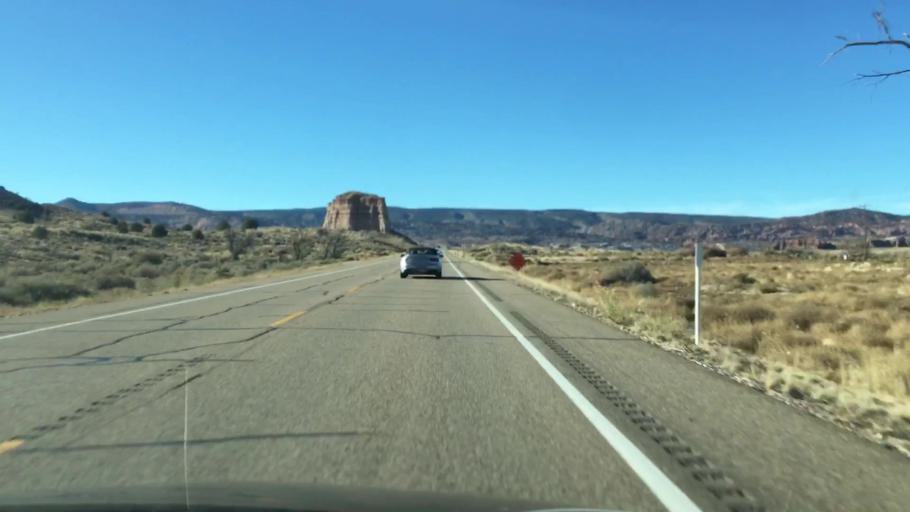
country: US
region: Arizona
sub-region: Coconino County
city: Page
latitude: 37.1089
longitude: -111.9131
